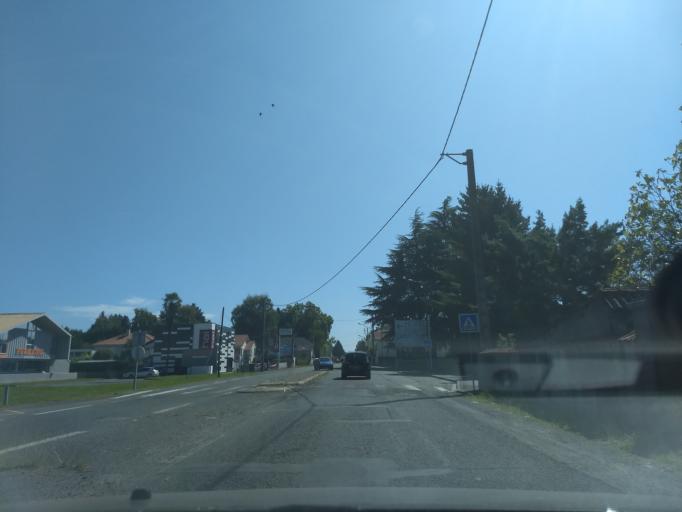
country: FR
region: Aquitaine
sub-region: Departement des Pyrenees-Atlantiques
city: Idron
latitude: 43.3023
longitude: -0.3182
